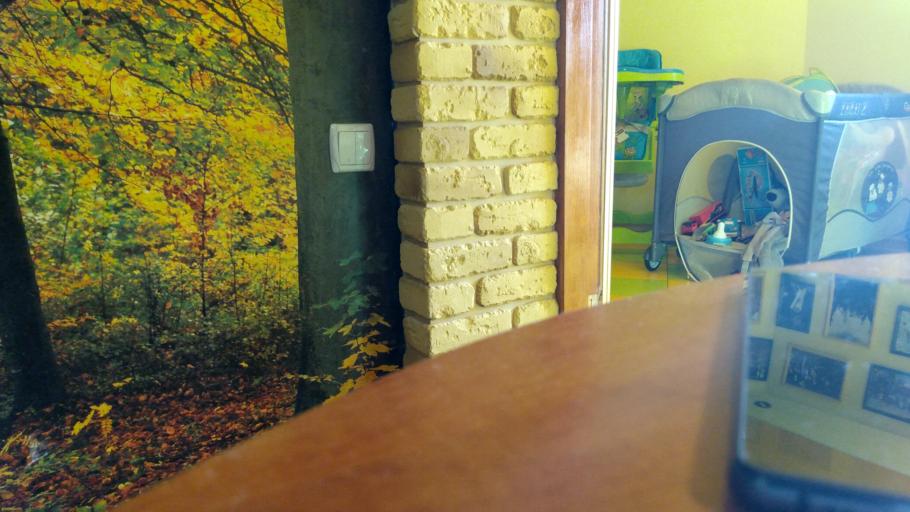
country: RU
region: Tverskaya
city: Likhoslavl'
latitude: 57.1541
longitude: 35.6014
